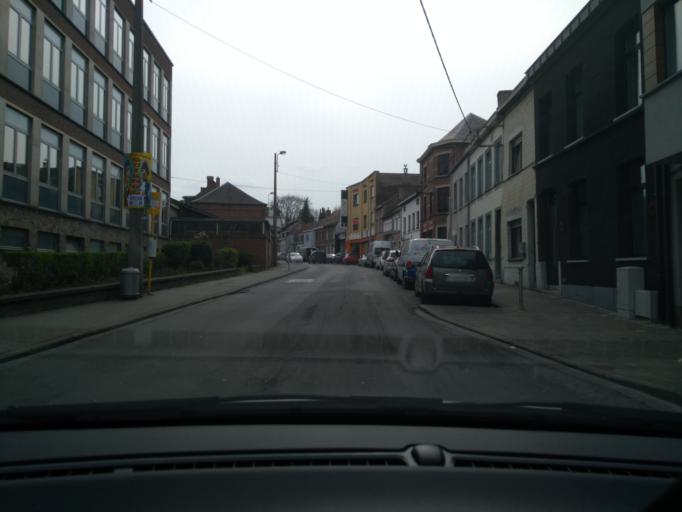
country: BE
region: Wallonia
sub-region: Province du Brabant Wallon
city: Nivelles
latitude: 50.5945
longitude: 4.3195
